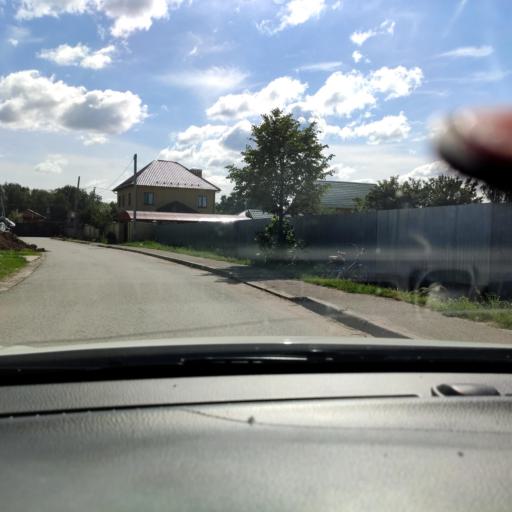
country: RU
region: Tatarstan
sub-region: Gorod Kazan'
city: Kazan
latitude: 55.7138
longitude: 49.1042
